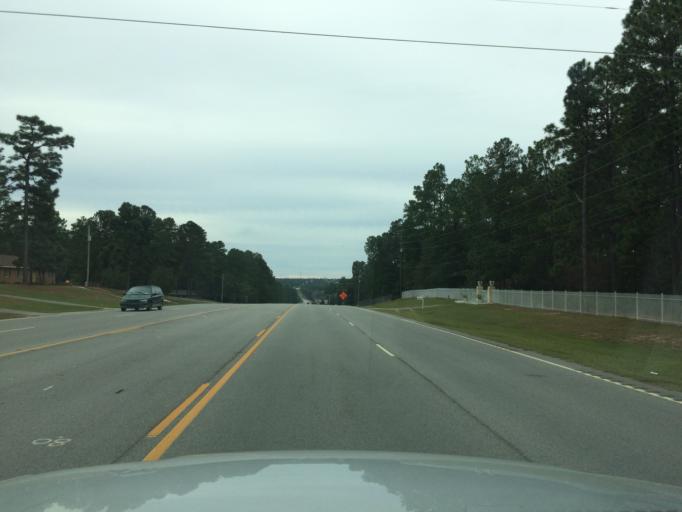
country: US
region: South Carolina
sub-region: Aiken County
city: Aiken
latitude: 33.6188
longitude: -81.6790
